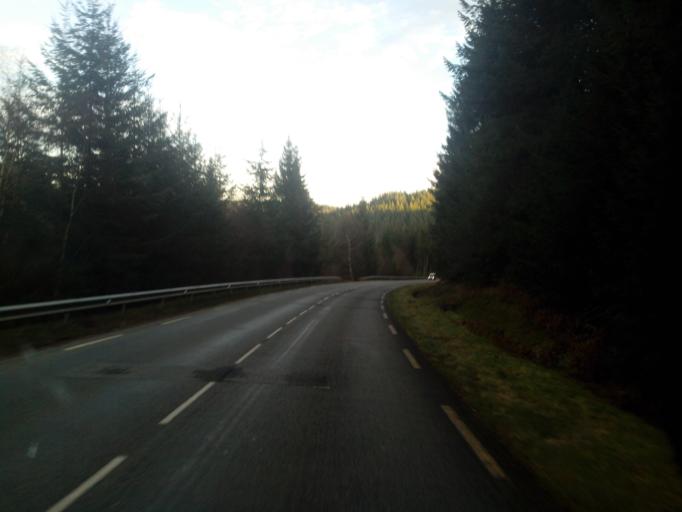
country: FR
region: Limousin
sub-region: Departement de la Correze
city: Meymac
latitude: 45.5798
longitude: 2.1166
